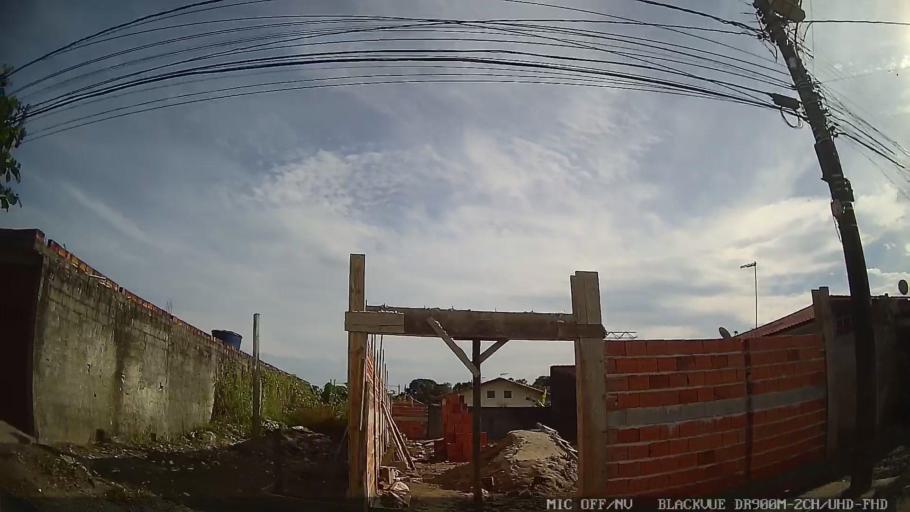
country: BR
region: Sao Paulo
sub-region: Itanhaem
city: Itanhaem
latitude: -24.1597
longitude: -46.7707
